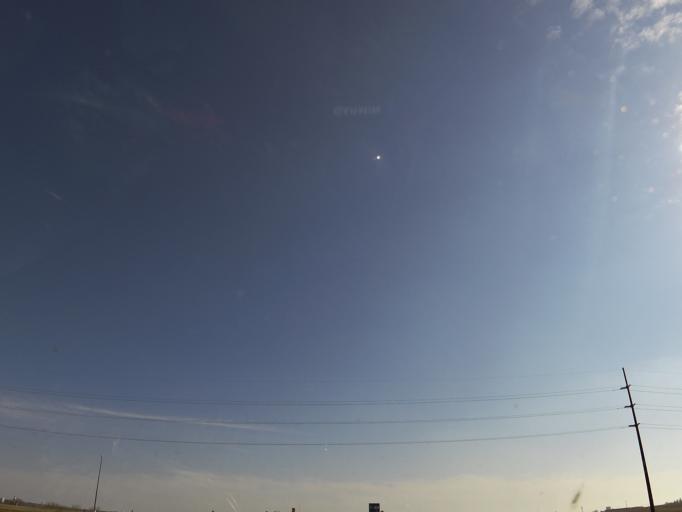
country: US
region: Minnesota
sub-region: Steele County
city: Owatonna
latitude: 44.1108
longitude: -93.2463
